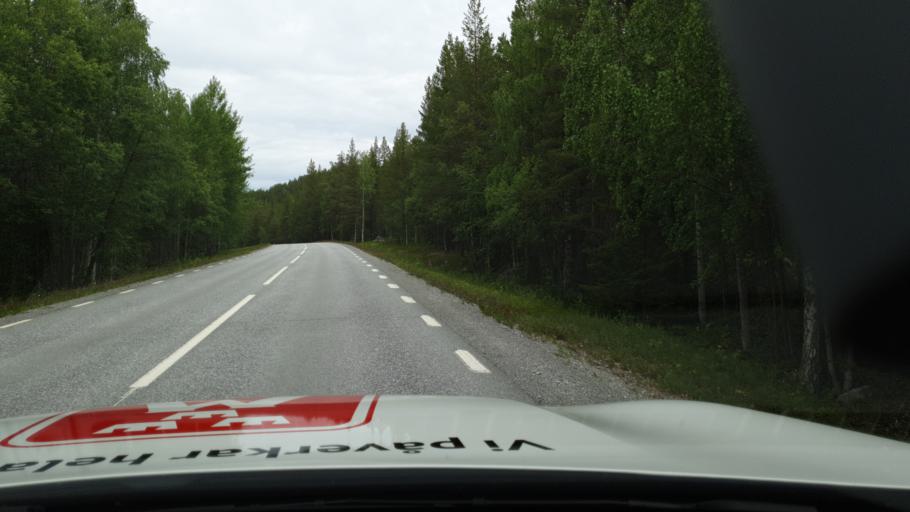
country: SE
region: Vaesterbotten
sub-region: Storumans Kommun
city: Storuman
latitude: 65.1556
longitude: 17.0620
